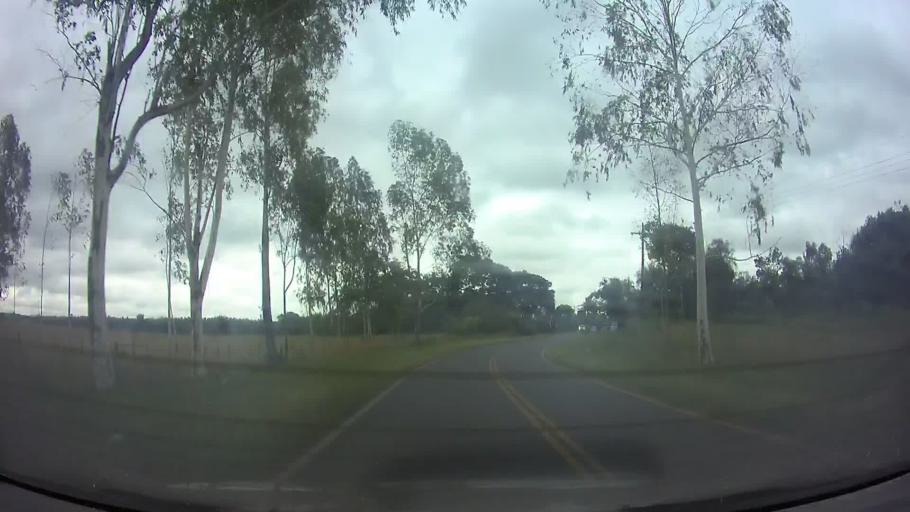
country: PY
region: Central
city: Nueva Italia
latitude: -25.5543
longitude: -57.5024
